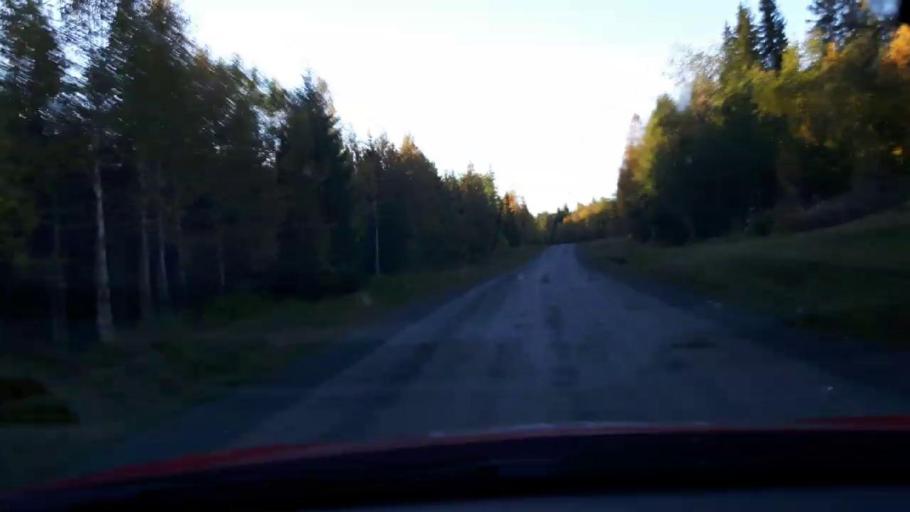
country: SE
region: Jaemtland
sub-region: Krokoms Kommun
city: Krokom
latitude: 63.4475
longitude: 14.5767
